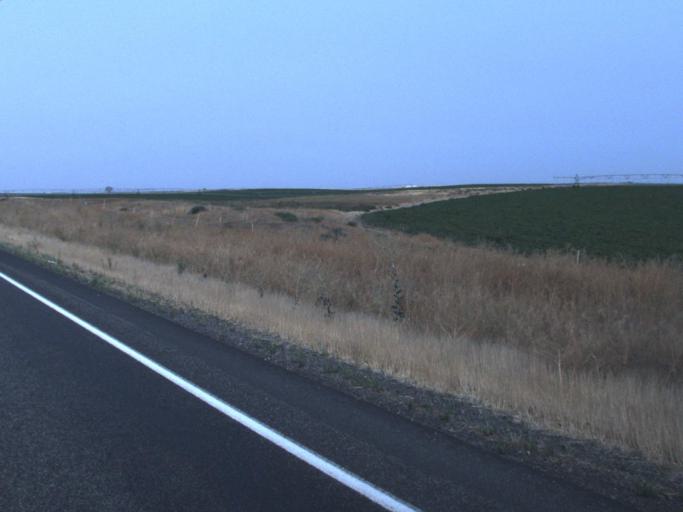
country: US
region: Oregon
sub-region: Morrow County
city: Irrigon
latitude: 45.9738
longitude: -119.6030
